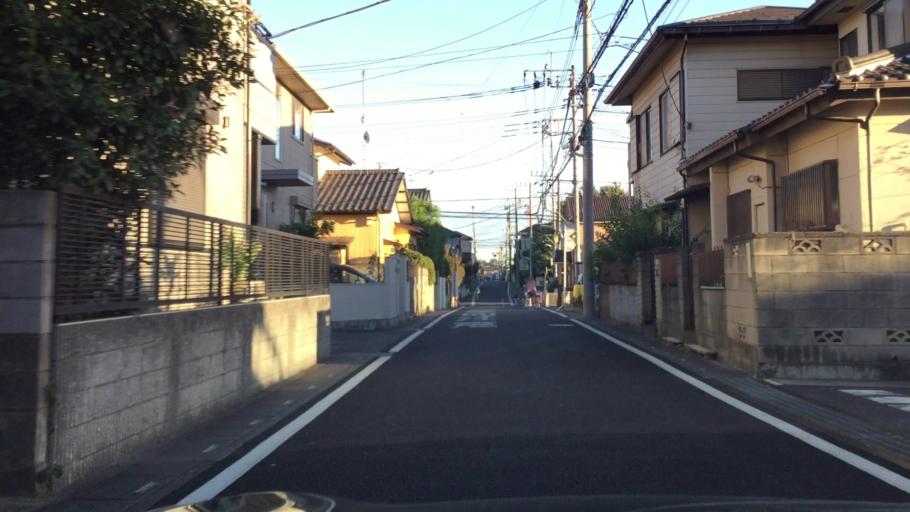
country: JP
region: Saitama
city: Ageoshimo
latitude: 35.9316
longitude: 139.6015
